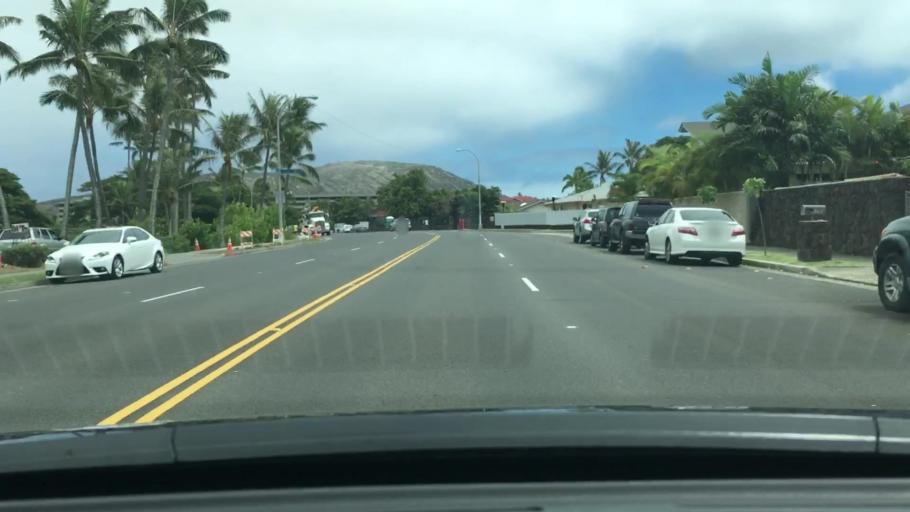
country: US
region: Hawaii
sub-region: Honolulu County
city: Waimanalo Beach
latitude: 21.2906
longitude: -157.7074
